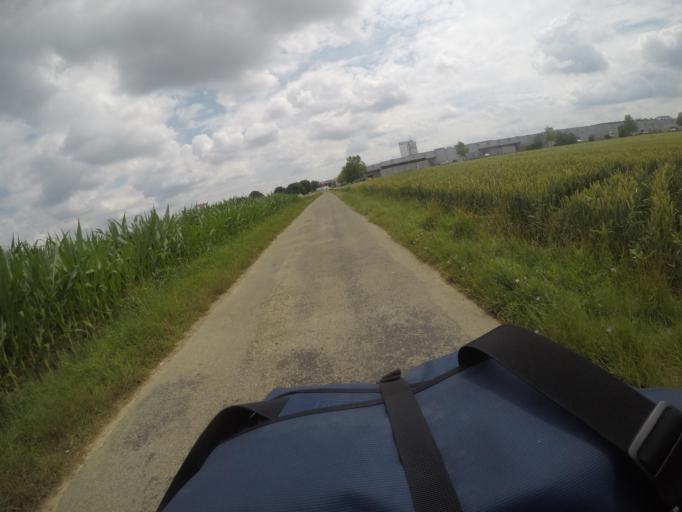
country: DE
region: Bavaria
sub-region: Swabia
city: Memmingen
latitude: 48.0058
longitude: 10.1677
